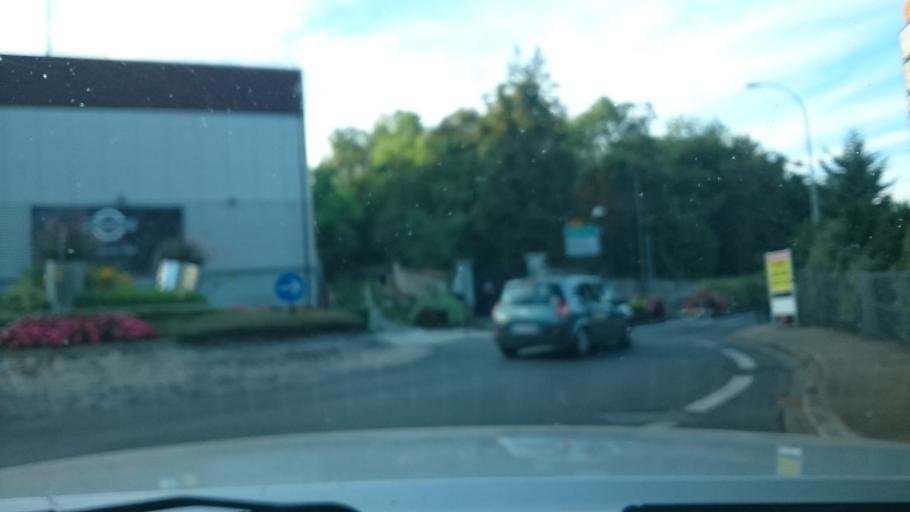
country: FR
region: Ile-de-France
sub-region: Departement de Seine-et-Marne
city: Samoreau
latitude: 48.4200
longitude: 2.7364
